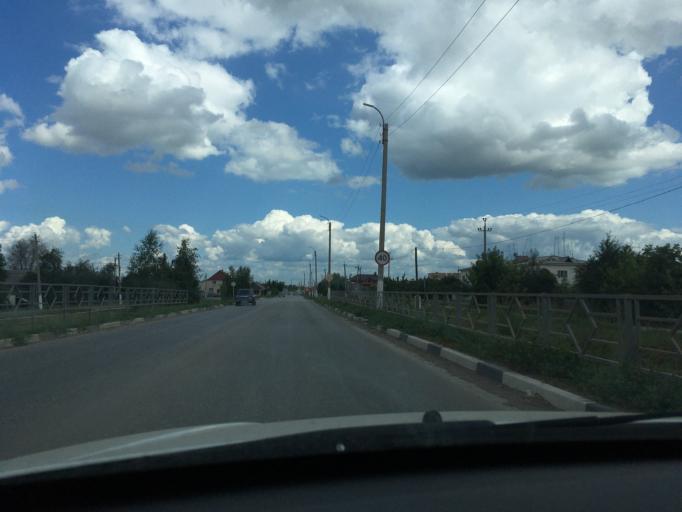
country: RU
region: Samara
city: Bezenchuk
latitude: 52.9875
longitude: 49.4348
